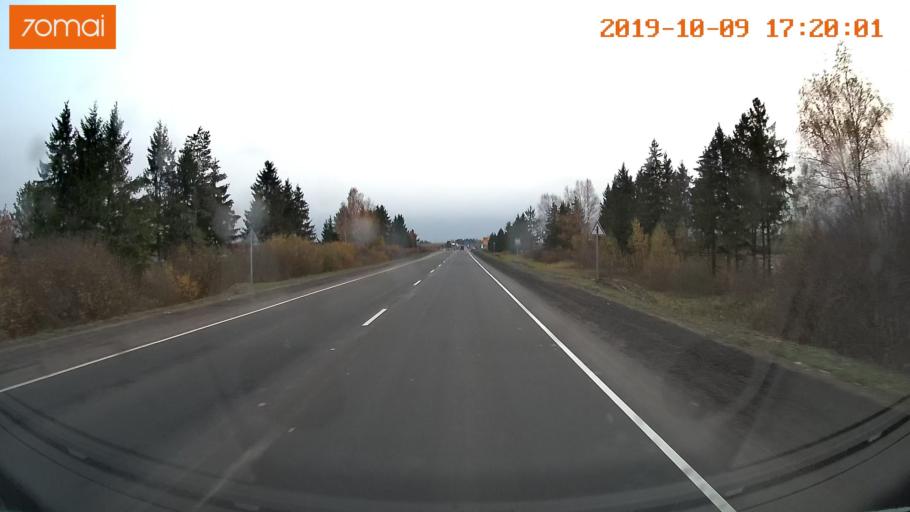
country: RU
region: Ivanovo
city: Furmanov
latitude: 57.2391
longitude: 41.1459
